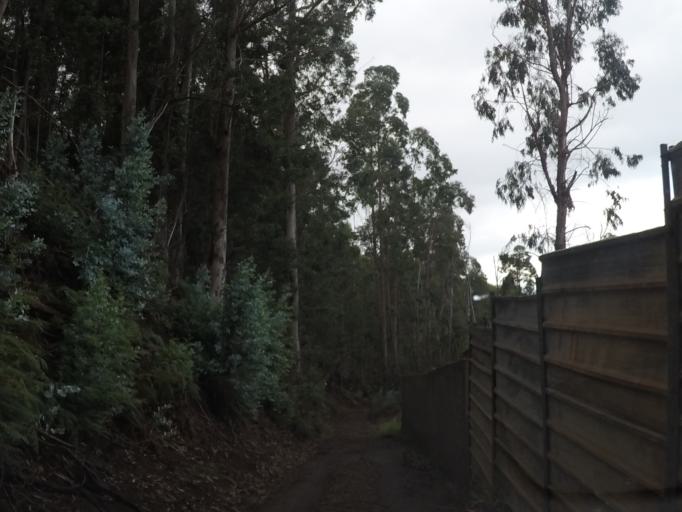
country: PT
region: Madeira
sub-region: Funchal
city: Nossa Senhora do Monte
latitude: 32.6780
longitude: -16.8775
